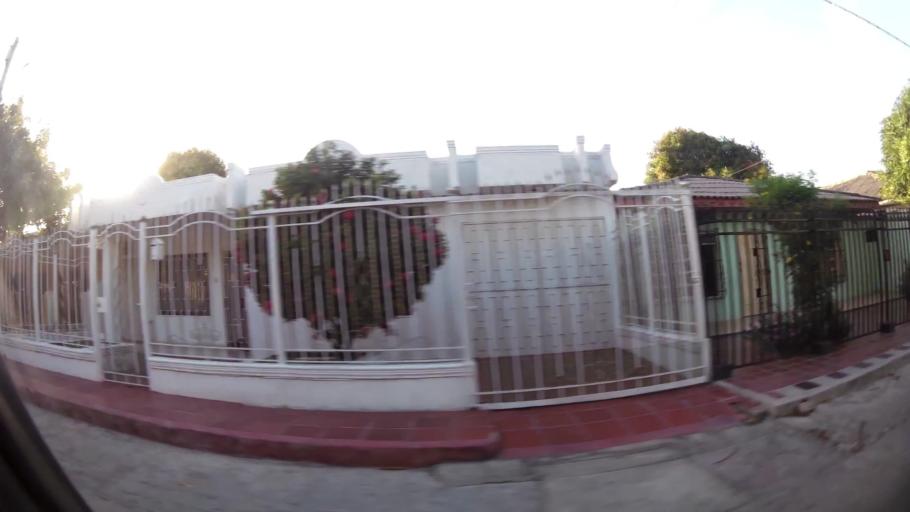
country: CO
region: Atlantico
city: Barranquilla
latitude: 10.9682
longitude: -74.7959
